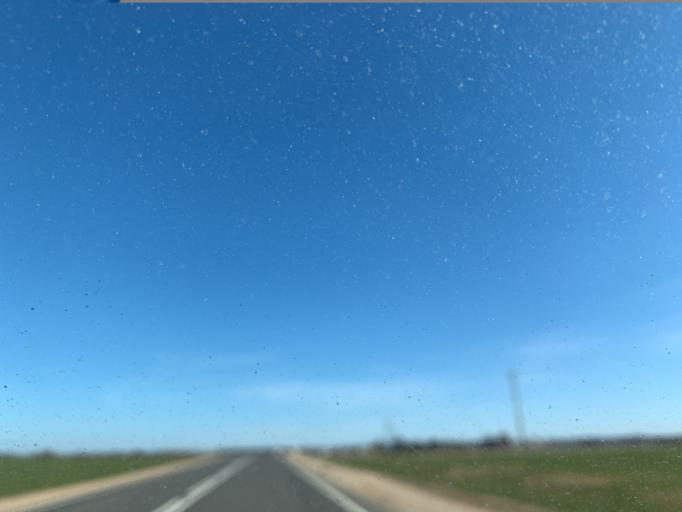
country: BY
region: Minsk
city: Nyasvizh
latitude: 53.2233
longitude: 26.7084
